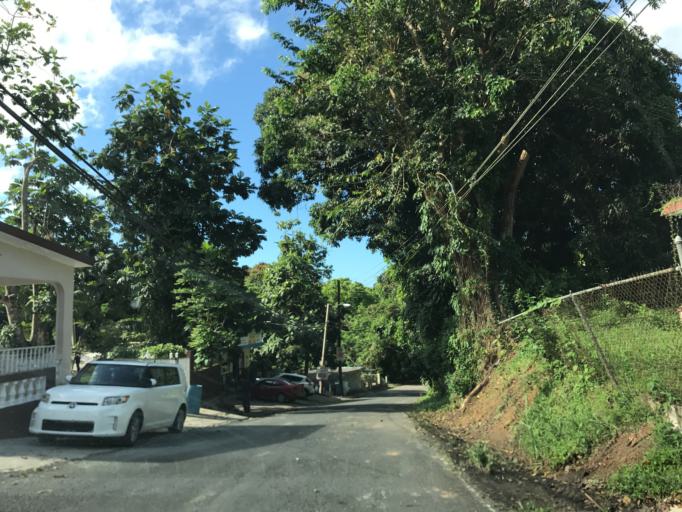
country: PR
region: Luquillo
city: Ramos
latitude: 18.3422
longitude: -65.7296
